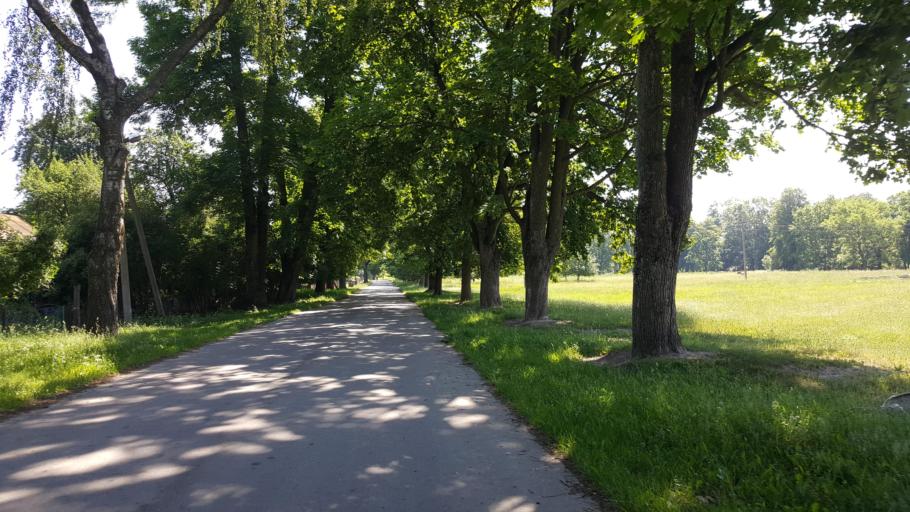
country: BY
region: Brest
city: Zhabinka
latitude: 52.2353
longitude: 24.0034
